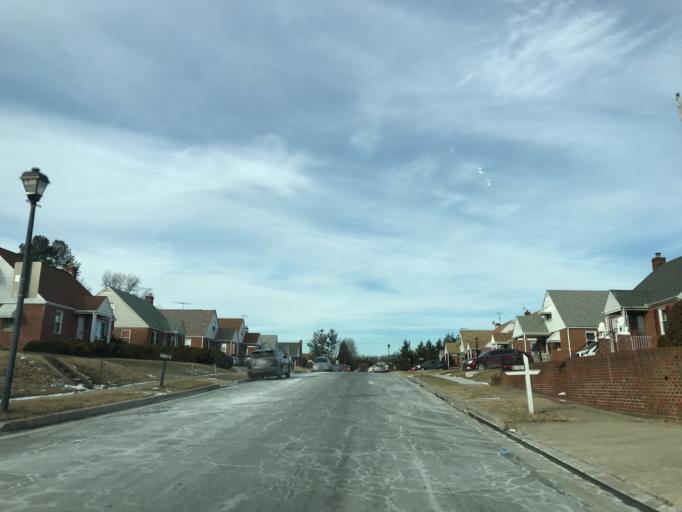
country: US
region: Maryland
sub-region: Baltimore County
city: Rosedale
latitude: 39.3402
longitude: -76.5165
